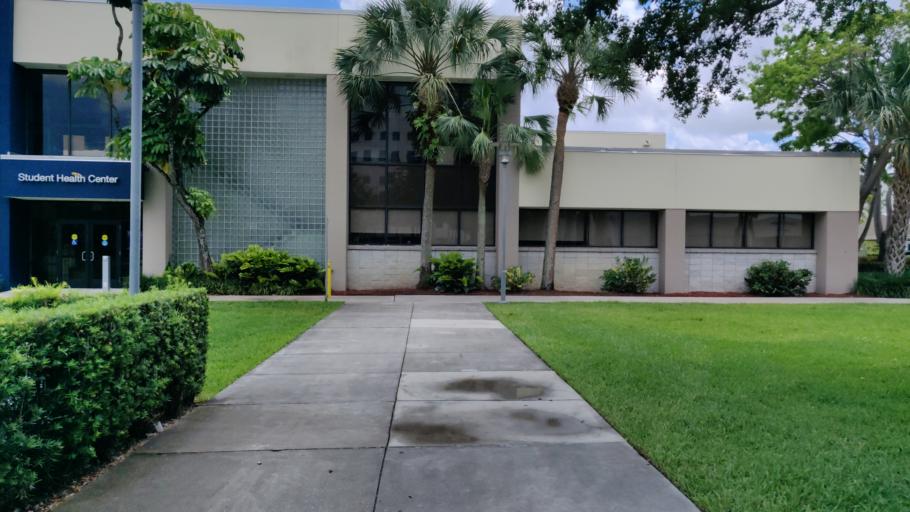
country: US
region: Florida
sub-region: Miami-Dade County
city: Sweetwater
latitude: 25.7564
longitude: -80.3768
